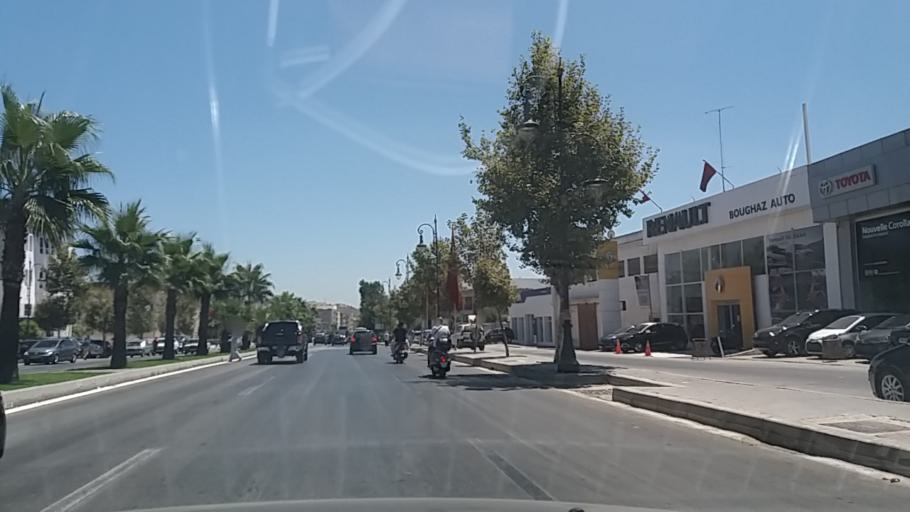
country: MA
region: Tanger-Tetouan
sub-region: Tanger-Assilah
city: Tangier
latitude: 35.7655
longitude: -5.7987
